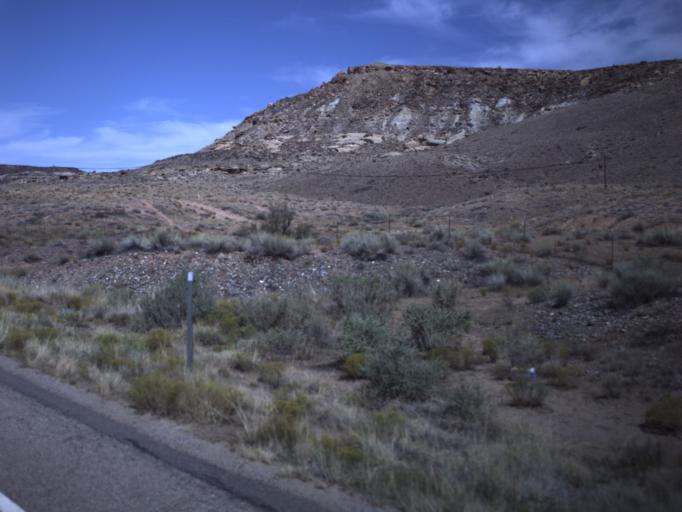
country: US
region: Colorado
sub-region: Montezuma County
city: Towaoc
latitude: 37.2115
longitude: -109.1736
